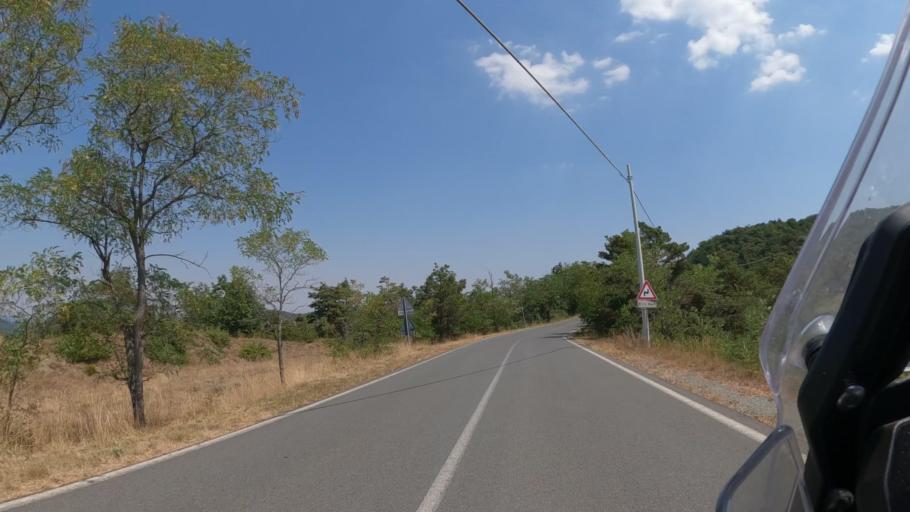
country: IT
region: Piedmont
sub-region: Provincia di Alessandria
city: Morbello
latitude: 44.5552
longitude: 8.5027
